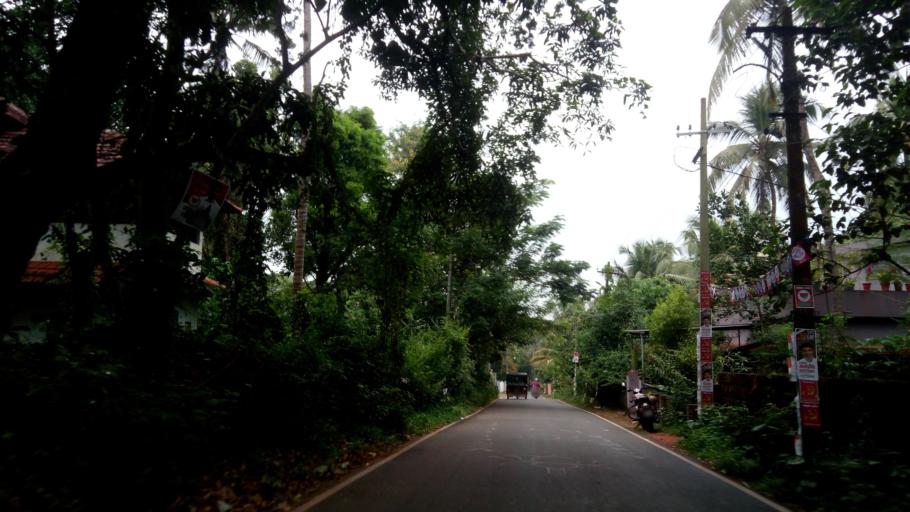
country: IN
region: Kerala
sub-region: Malappuram
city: Malappuram
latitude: 10.9874
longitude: 76.0072
